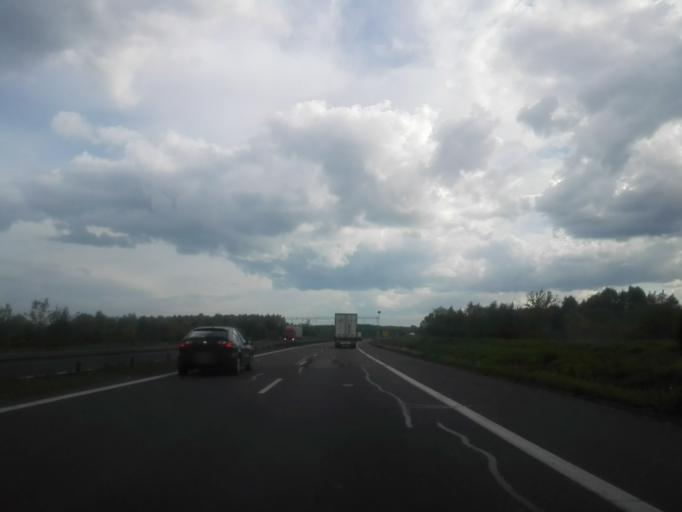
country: PL
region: Masovian Voivodeship
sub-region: Powiat ostrowski
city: Ostrow Mazowiecka
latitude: 52.8104
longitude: 21.8771
